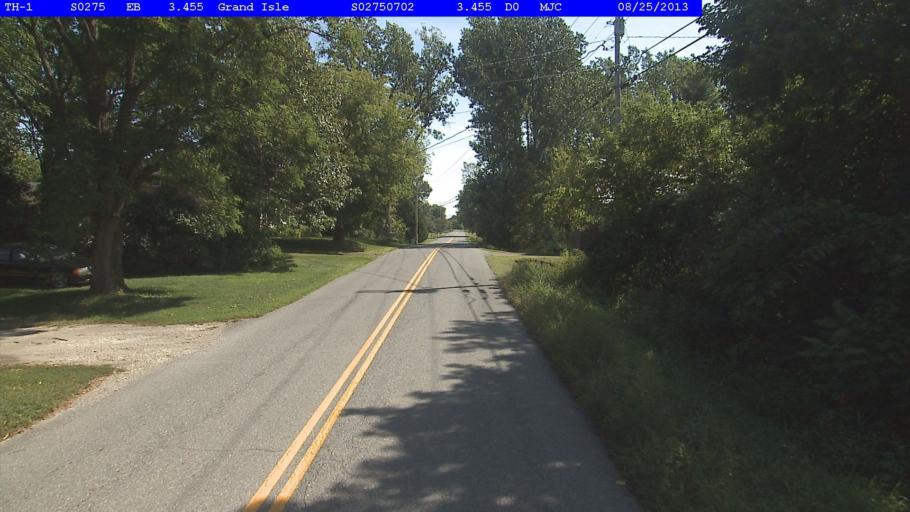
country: US
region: Vermont
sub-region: Grand Isle County
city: North Hero
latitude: 44.7354
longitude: -73.3119
